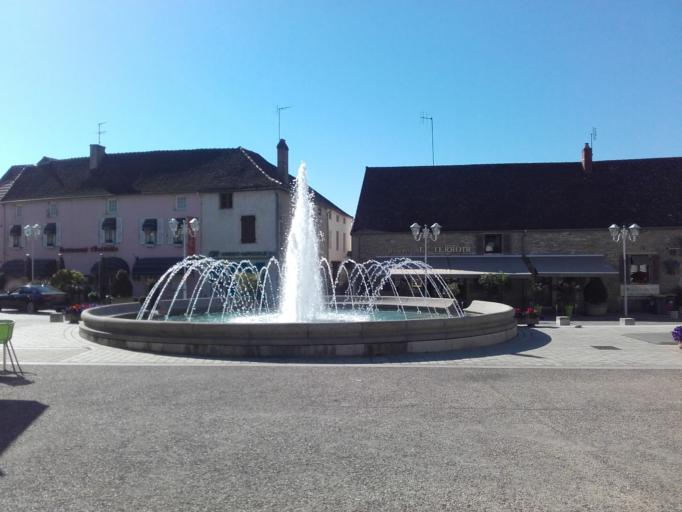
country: FR
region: Bourgogne
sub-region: Departement de Saone-et-Loire
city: Chagny
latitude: 46.9115
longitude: 4.6997
